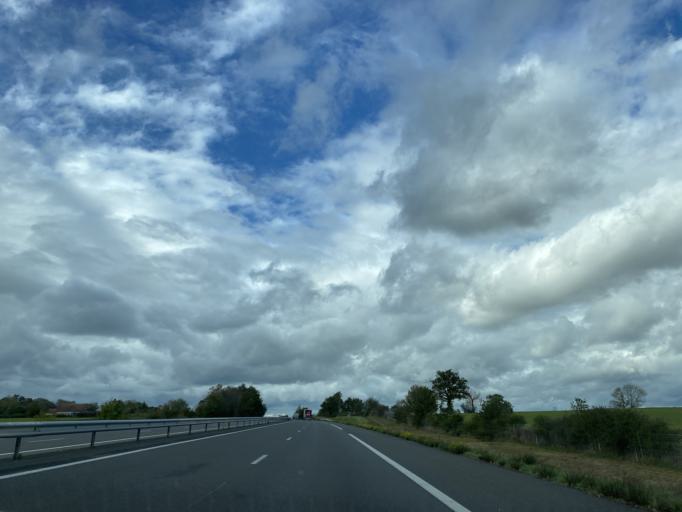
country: FR
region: Auvergne
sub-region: Departement de l'Allier
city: Montmarault
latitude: 46.2933
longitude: 3.0367
